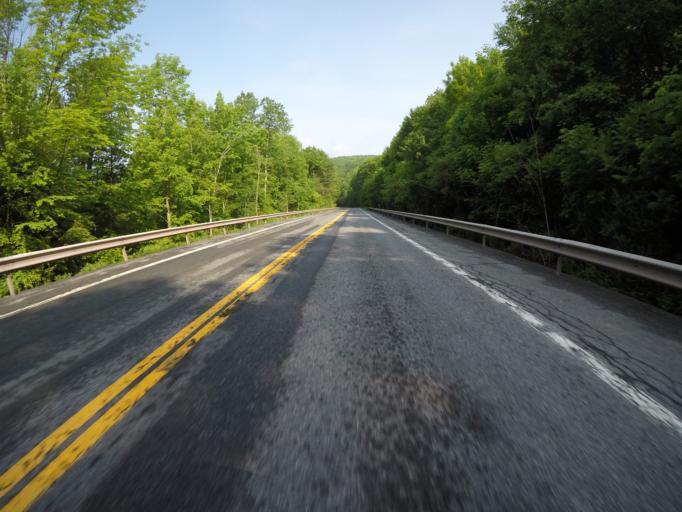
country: US
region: New York
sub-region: Sullivan County
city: Livingston Manor
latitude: 42.1261
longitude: -74.7071
